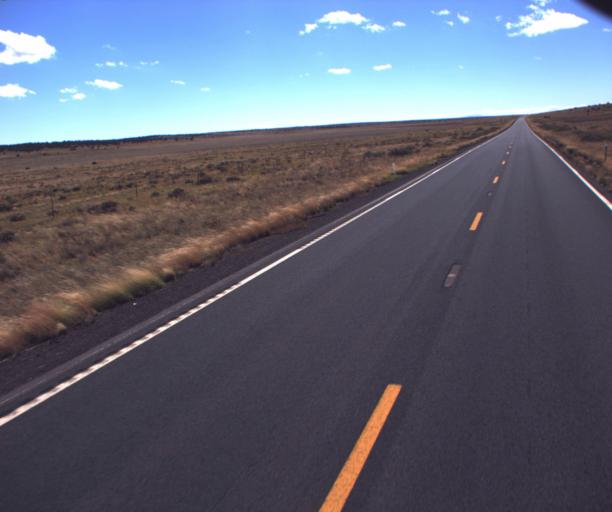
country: US
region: Arizona
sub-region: Apache County
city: Houck
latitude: 34.9881
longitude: -109.2271
